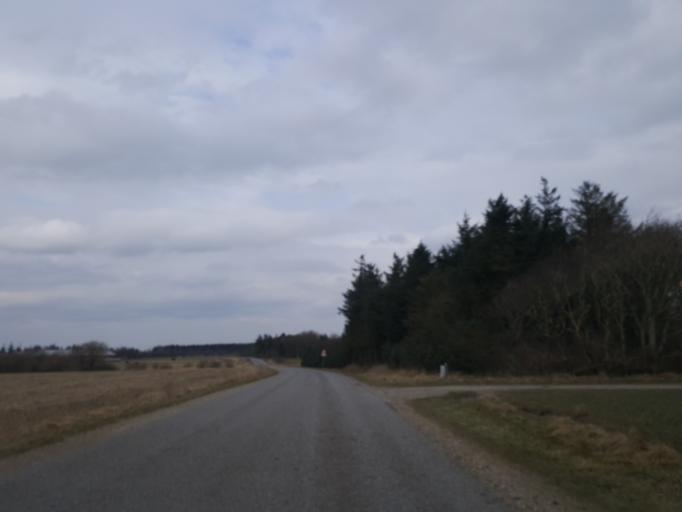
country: DK
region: Central Jutland
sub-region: Holstebro Kommune
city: Ulfborg
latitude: 56.3447
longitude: 8.3051
